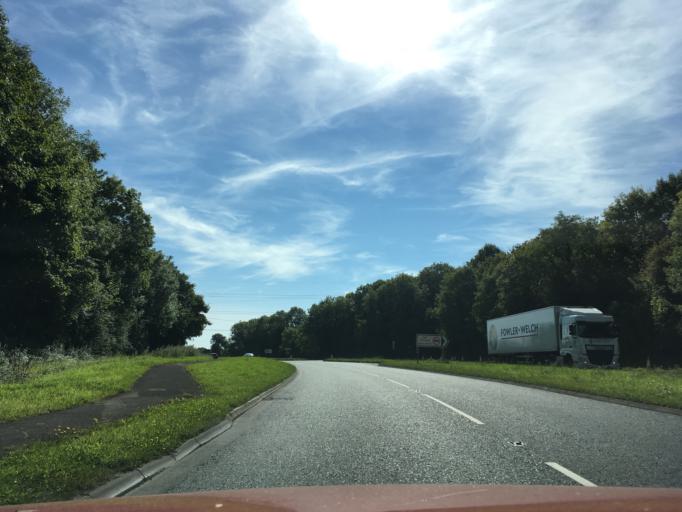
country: GB
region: England
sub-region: South Gloucestershire
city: Severn Beach
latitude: 51.5999
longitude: -2.6191
